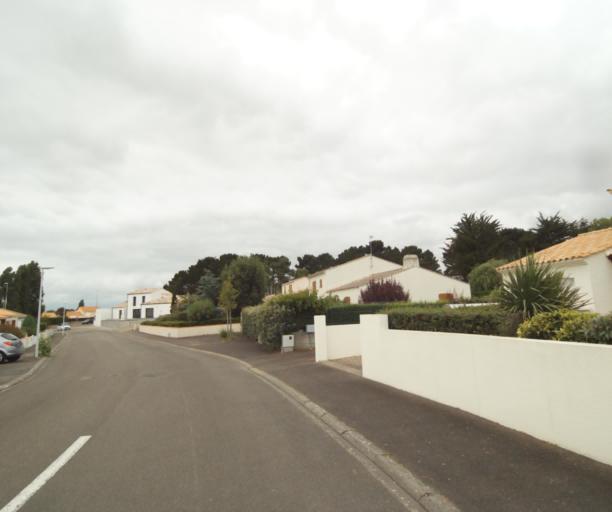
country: FR
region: Pays de la Loire
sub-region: Departement de la Vendee
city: Chateau-d'Olonne
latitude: 46.4856
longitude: -1.7490
